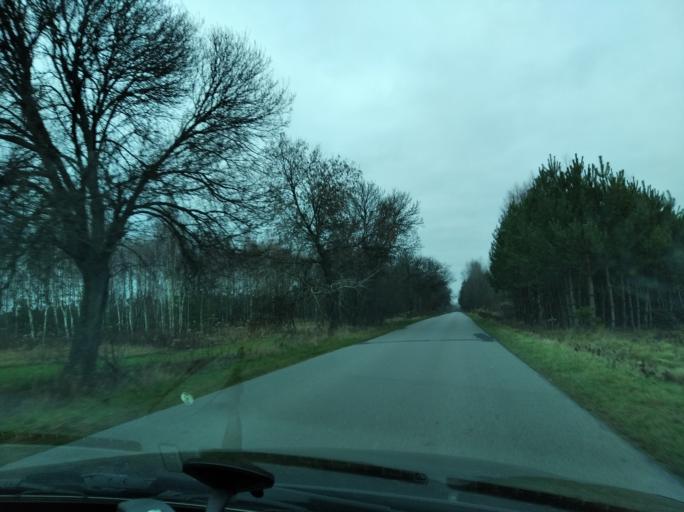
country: PL
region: Subcarpathian Voivodeship
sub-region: Powiat lancucki
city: Rakszawa
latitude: 50.1799
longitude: 22.2444
